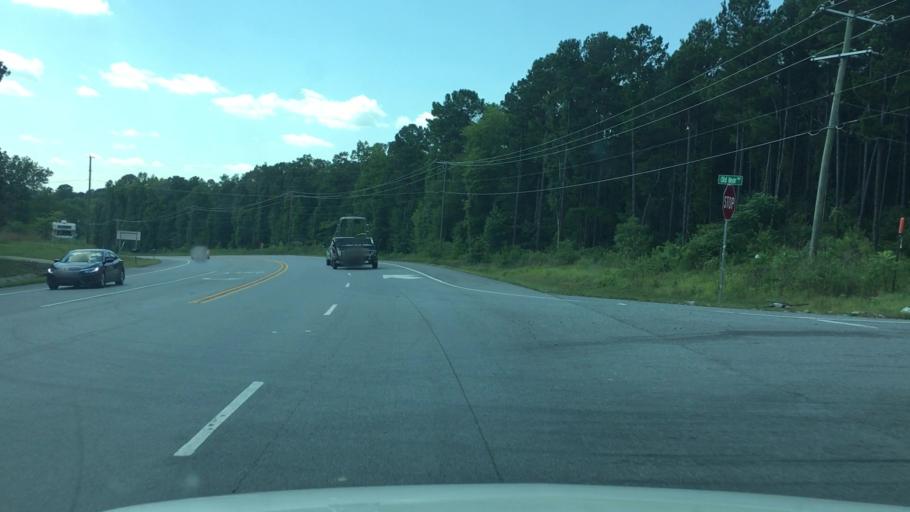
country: US
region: Arkansas
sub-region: Garland County
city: Piney
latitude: 34.5096
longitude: -93.1928
